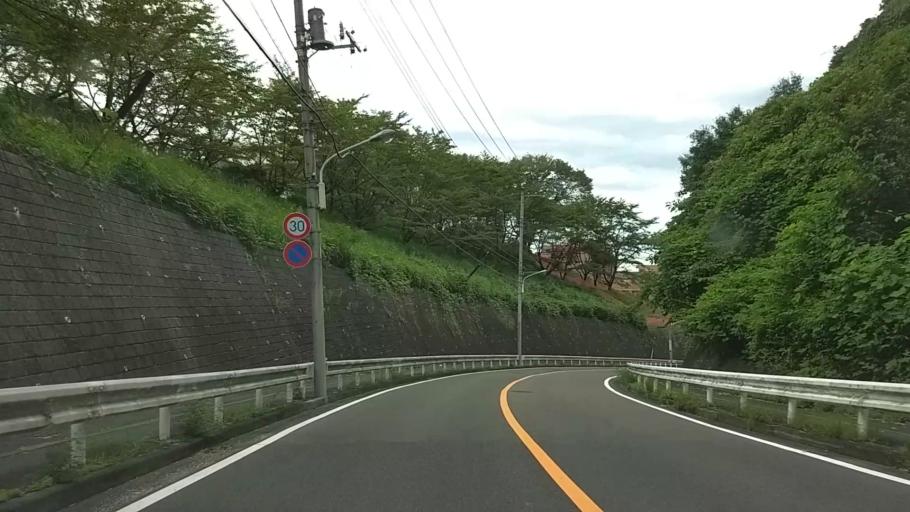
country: JP
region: Tokyo
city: Hachioji
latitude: 35.6293
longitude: 139.2896
